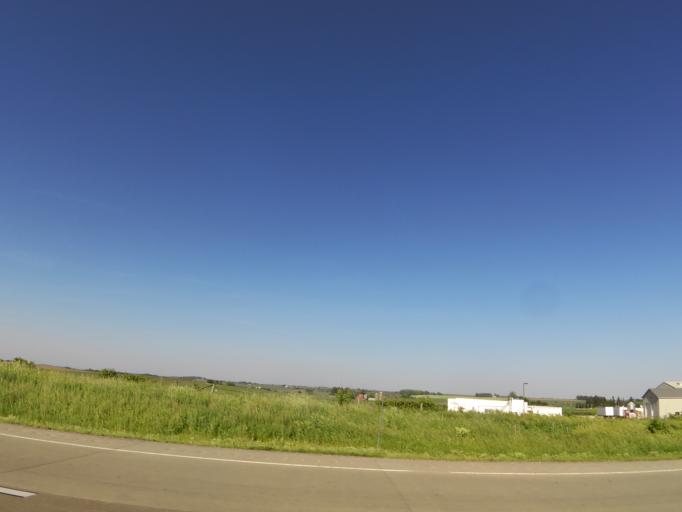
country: US
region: Wisconsin
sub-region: Columbia County
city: Poynette
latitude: 43.3396
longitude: -89.4553
